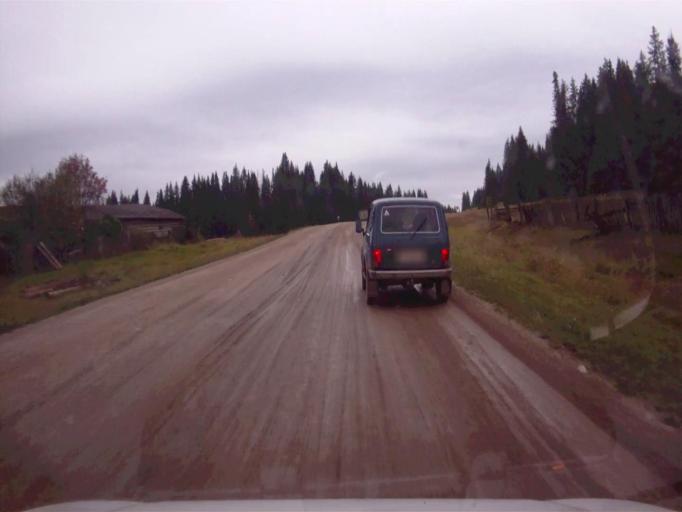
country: RU
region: Chelyabinsk
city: Nyazepetrovsk
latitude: 56.0609
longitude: 59.5633
